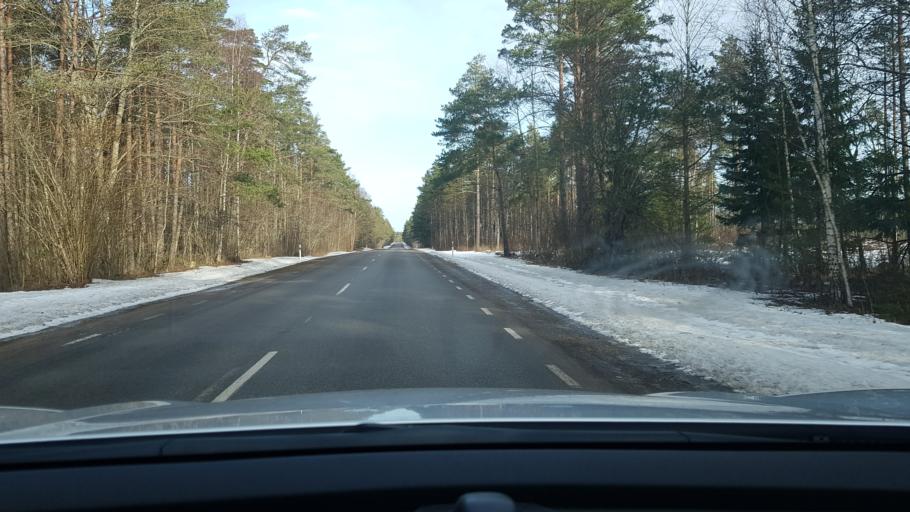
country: EE
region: Saare
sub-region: Kuressaare linn
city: Kuressaare
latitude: 58.4690
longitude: 22.7024
